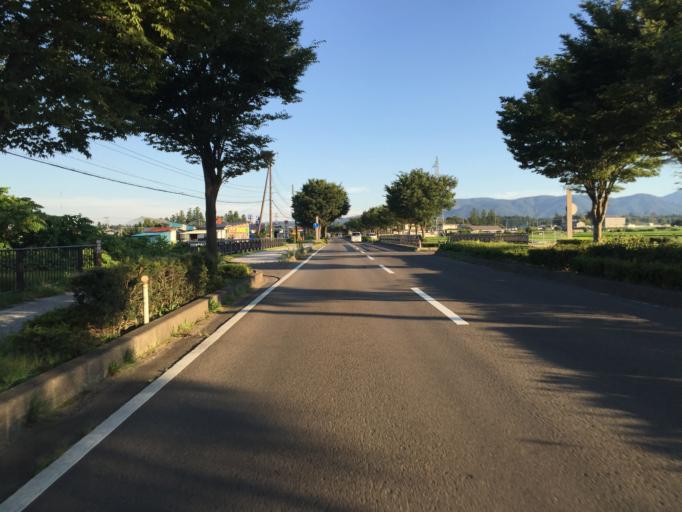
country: JP
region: Fukushima
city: Fukushima-shi
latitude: 37.7447
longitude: 140.3818
